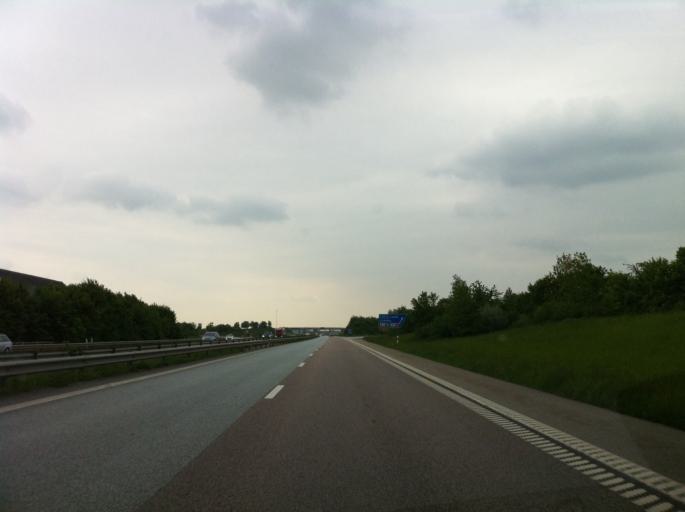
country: SE
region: Skane
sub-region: Lomma Kommun
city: Lomma
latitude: 55.6917
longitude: 13.0975
